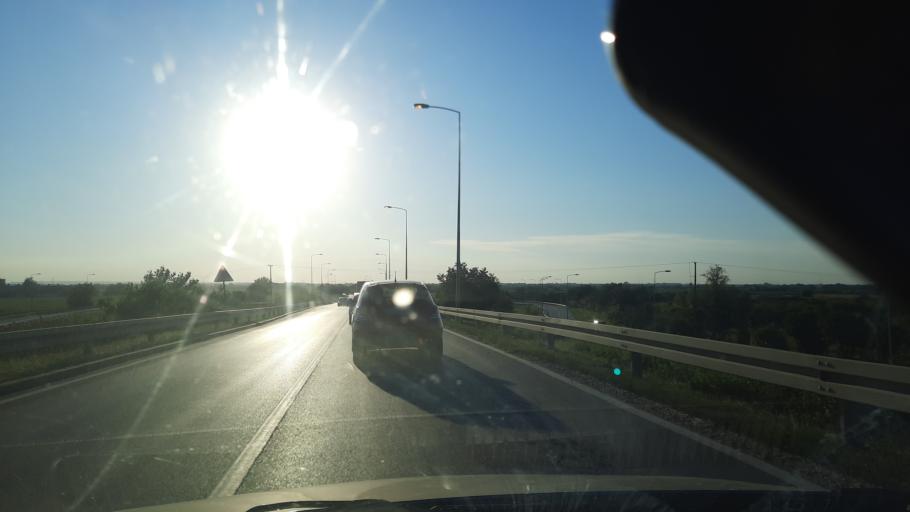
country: RS
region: Central Serbia
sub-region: Branicevski Okrug
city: Pozarevac
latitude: 44.5985
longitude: 21.1516
